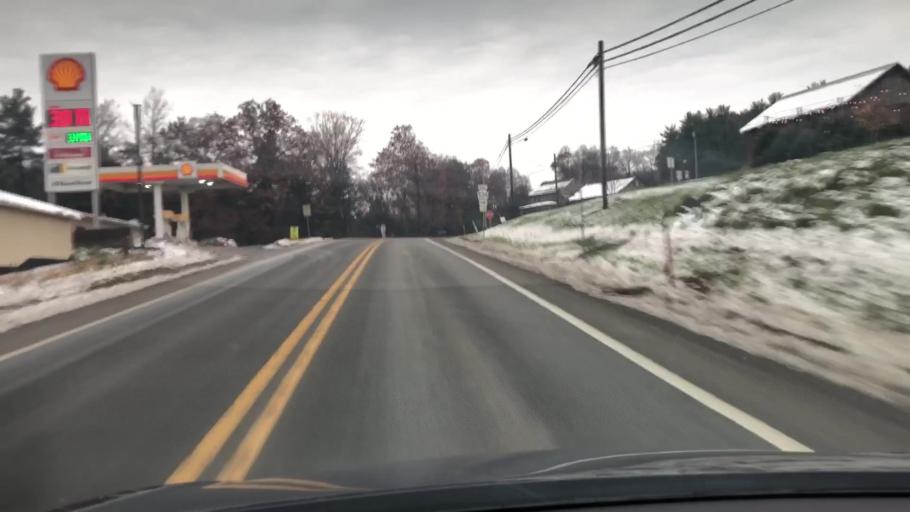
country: US
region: Pennsylvania
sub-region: Jefferson County
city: Brookville
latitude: 41.0391
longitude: -79.2577
